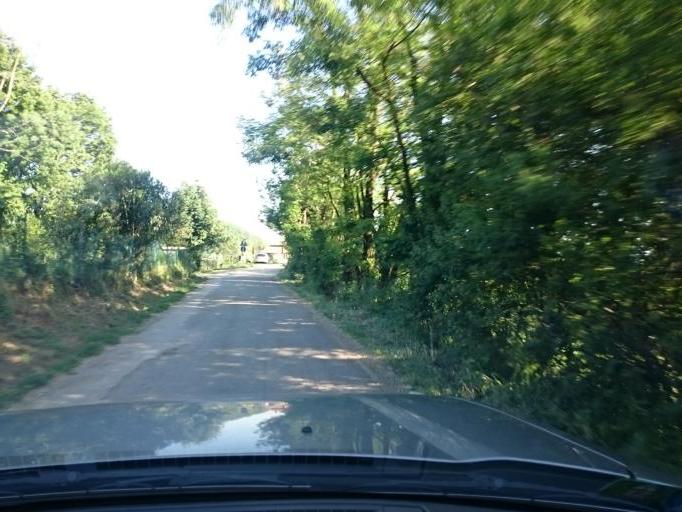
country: IT
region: Veneto
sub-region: Provincia di Padova
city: Galzignano
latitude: 45.2941
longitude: 11.7077
